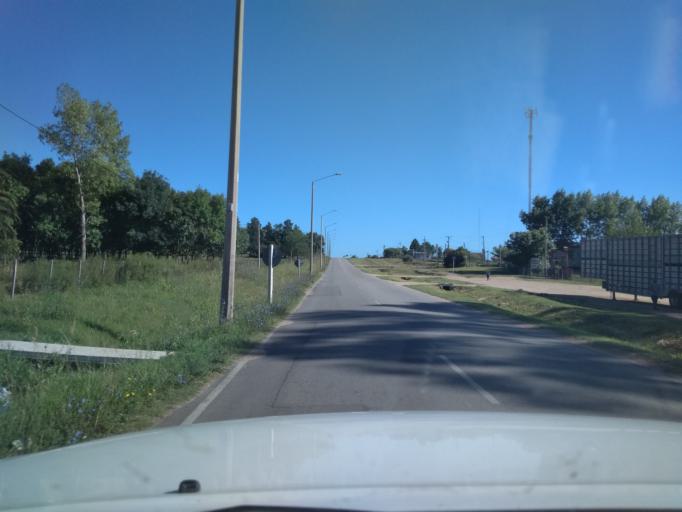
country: UY
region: Canelones
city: San Ramon
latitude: -34.3080
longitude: -55.9585
